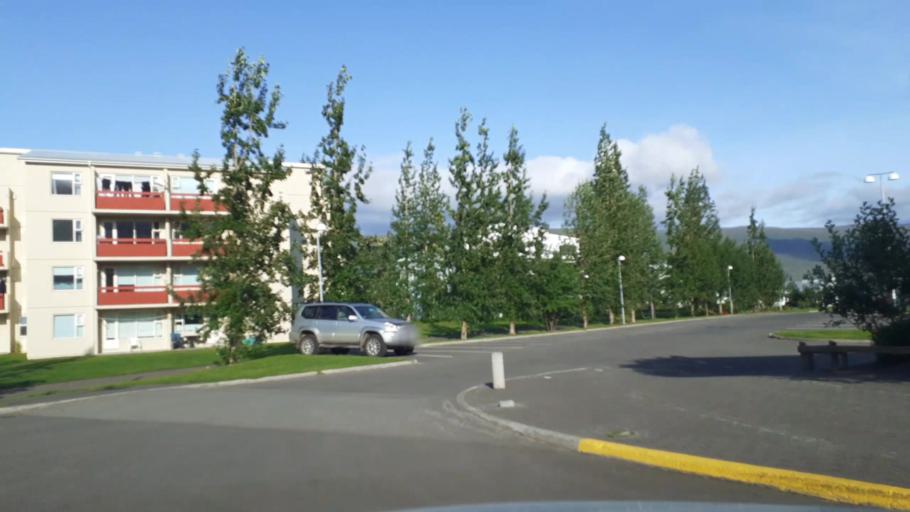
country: IS
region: Northeast
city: Akureyri
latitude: 65.6930
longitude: -18.1373
